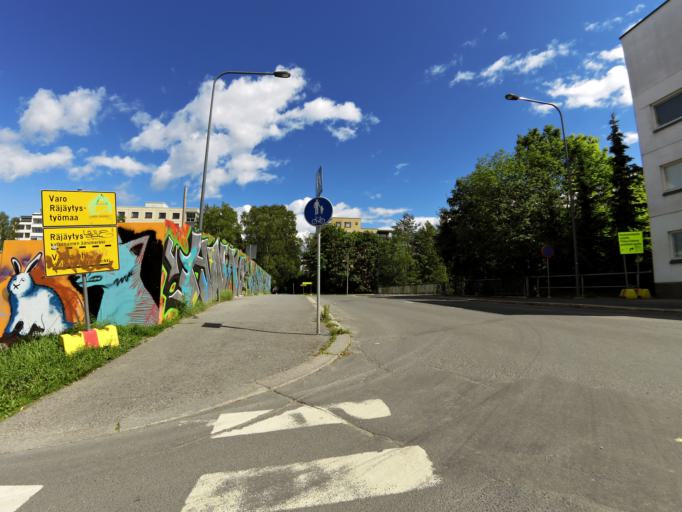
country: FI
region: Pirkanmaa
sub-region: Tampere
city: Tampere
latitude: 61.5057
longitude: 23.7725
